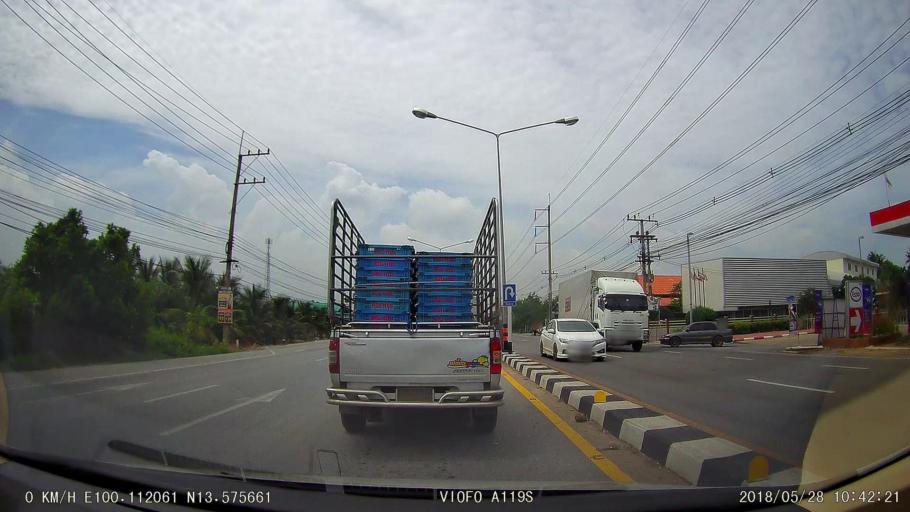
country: TH
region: Samut Sakhon
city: Ban Phaeo
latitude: 13.5836
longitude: 100.1084
